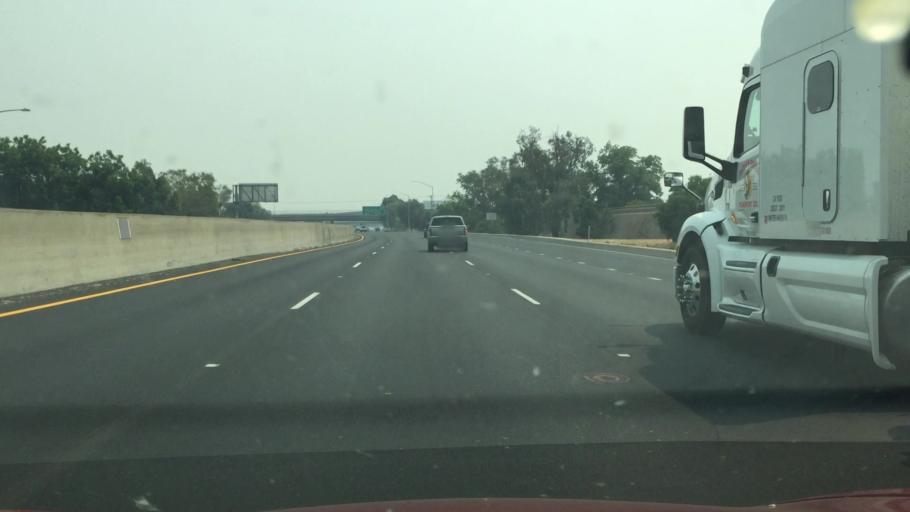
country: US
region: California
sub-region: San Joaquin County
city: Garden Acres
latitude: 37.9687
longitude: -121.2454
